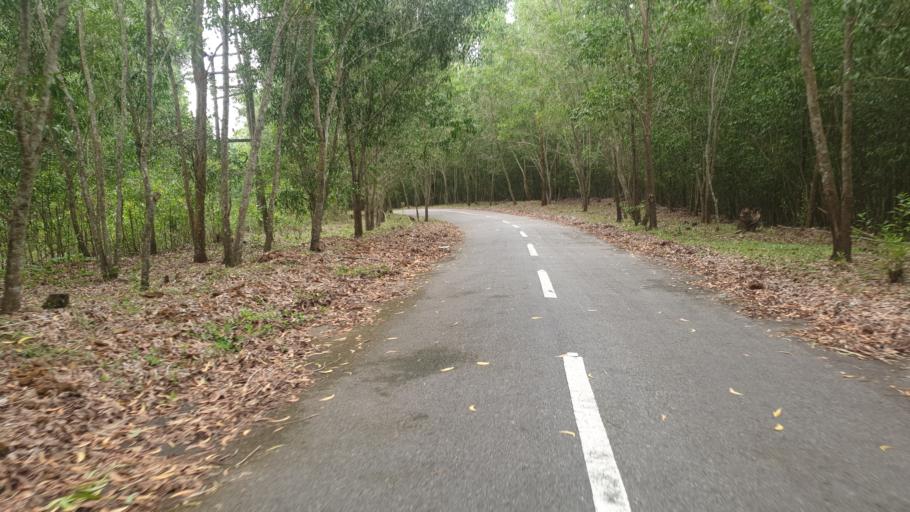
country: IN
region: Kerala
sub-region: Thiruvananthapuram
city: Nedumangad
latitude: 8.6323
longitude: 77.1173
